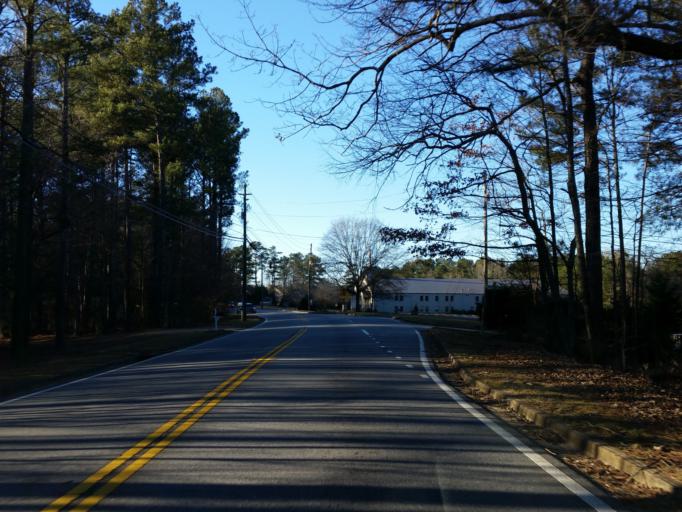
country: US
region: Georgia
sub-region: Cobb County
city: Acworth
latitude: 33.9694
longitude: -84.7087
